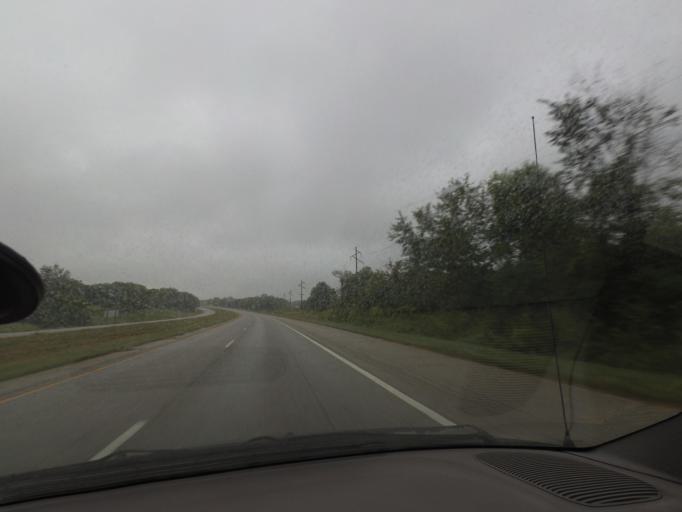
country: US
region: Illinois
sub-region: Pike County
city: Barry
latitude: 39.7106
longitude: -91.0584
